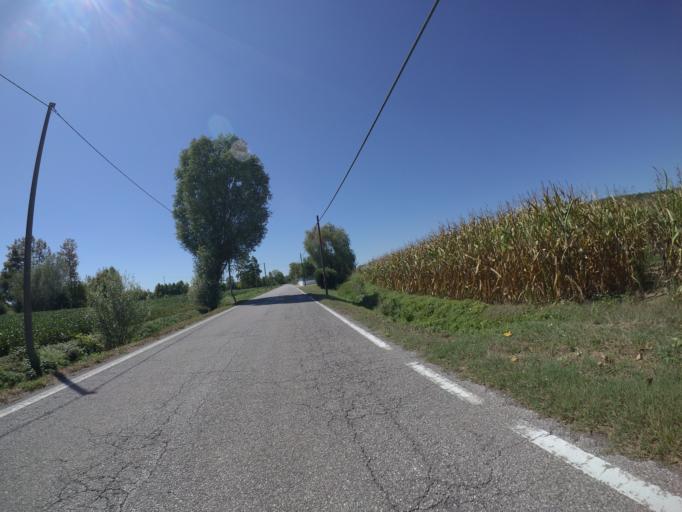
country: IT
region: Friuli Venezia Giulia
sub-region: Provincia di Udine
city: Rivignano
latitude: 45.8663
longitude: 13.0318
